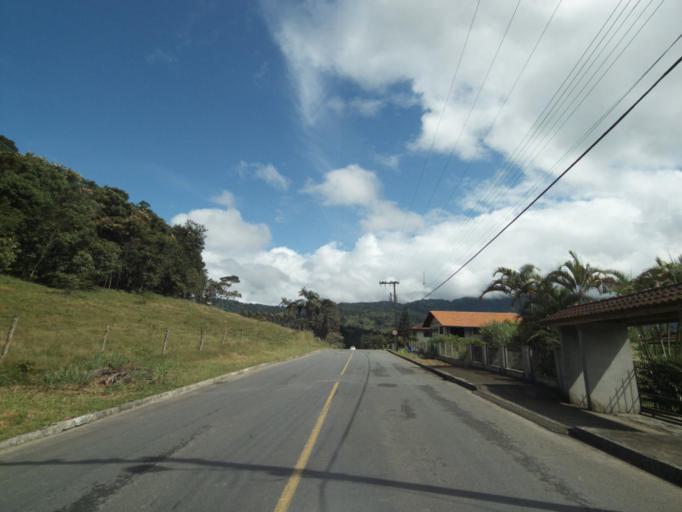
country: BR
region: Santa Catarina
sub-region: Pomerode
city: Pomerode
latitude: -26.6878
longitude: -49.1667
